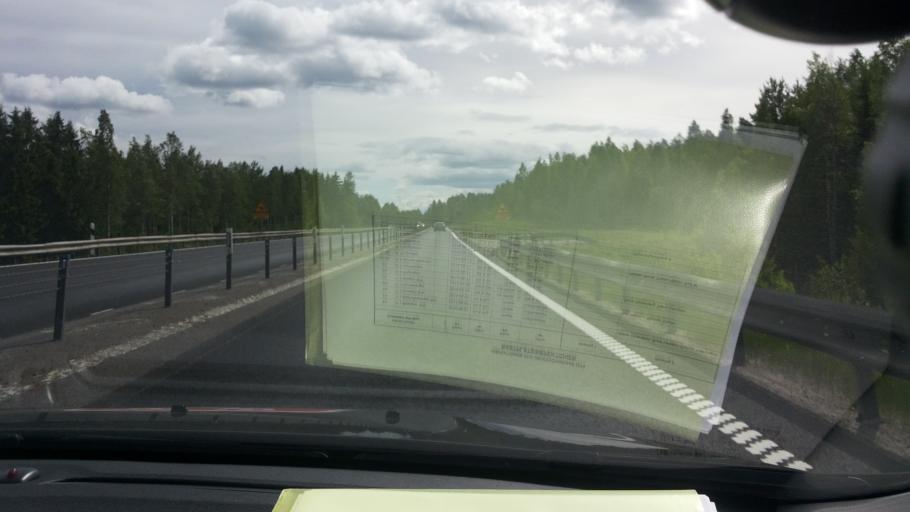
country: SE
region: Vaesternorrland
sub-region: Sundsvalls Kommun
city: Njurundabommen
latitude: 62.1734
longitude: 17.3566
